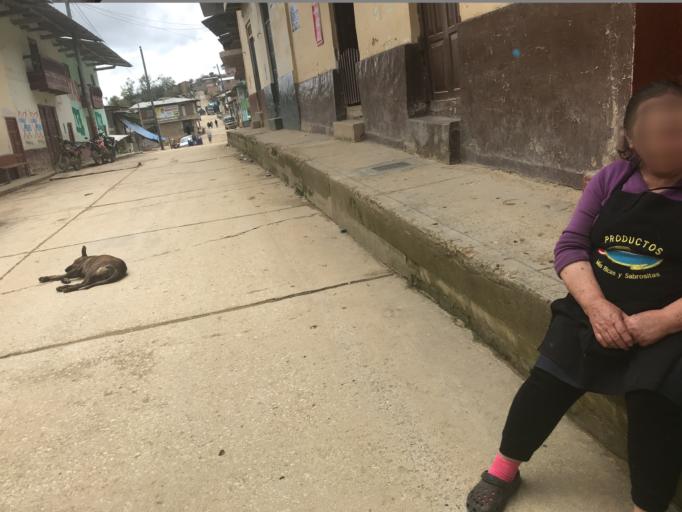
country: PE
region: Cajamarca
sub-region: Provincia de Chota
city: Querocoto
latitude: -6.3599
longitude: -79.0340
